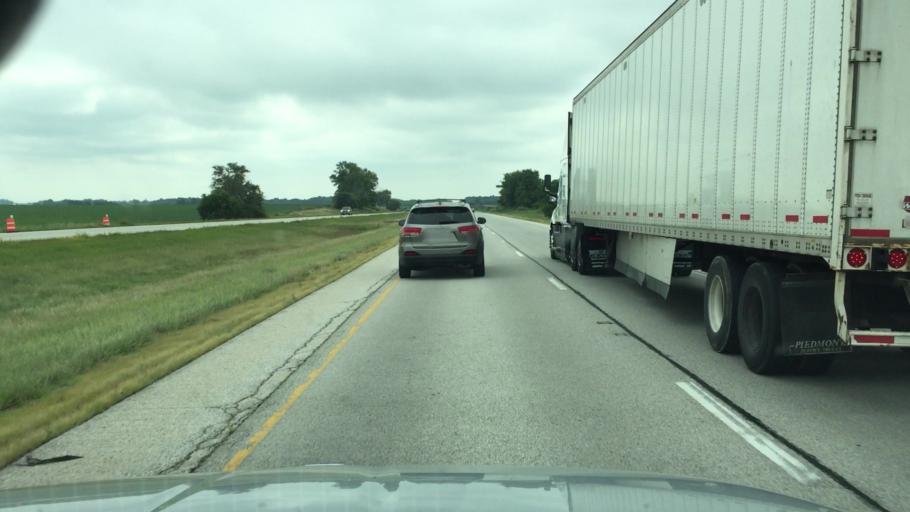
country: US
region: Illinois
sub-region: Knox County
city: Galesburg
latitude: 41.0928
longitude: -90.3333
